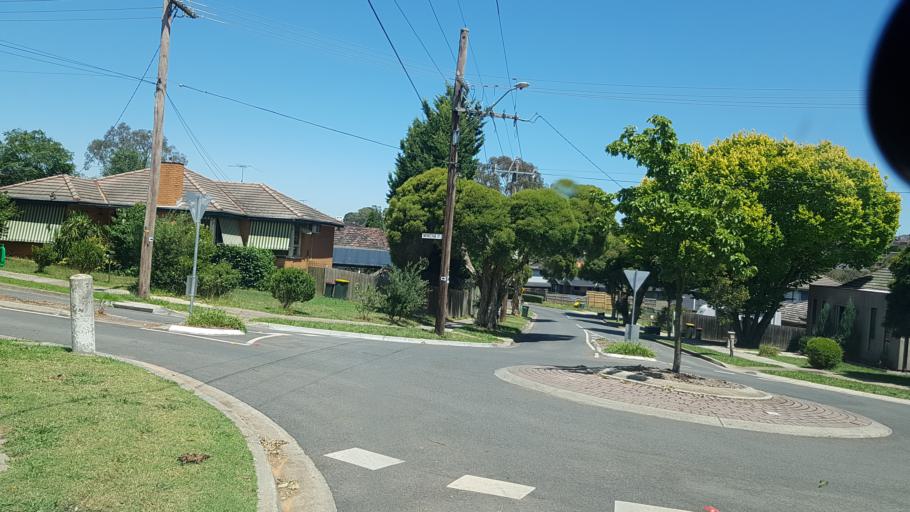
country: AU
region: Victoria
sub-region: Manningham
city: Templestowe Lower
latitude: -37.7614
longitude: 145.1010
